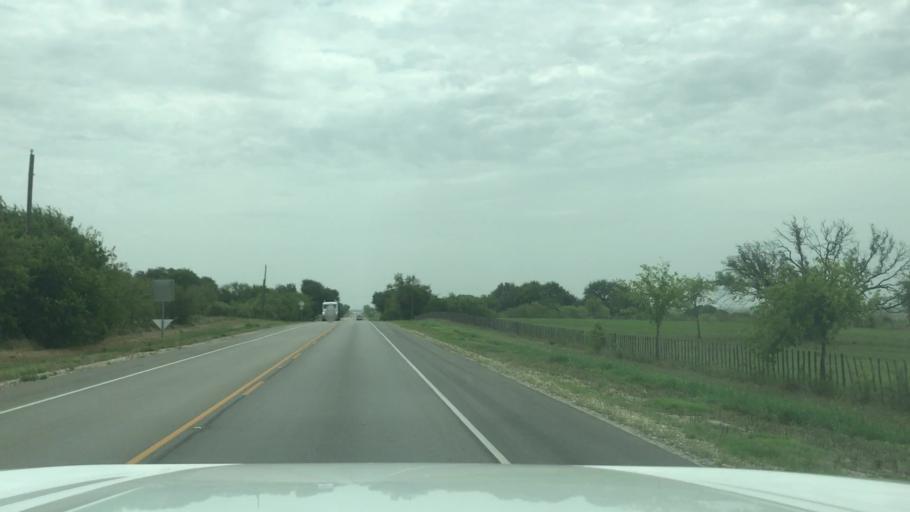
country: US
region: Texas
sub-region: Erath County
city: Dublin
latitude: 32.0852
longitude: -98.2530
